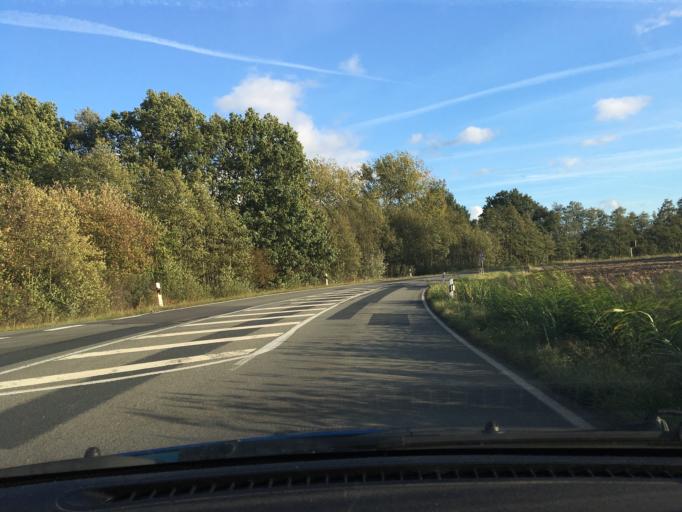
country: DE
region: Lower Saxony
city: Hittbergen
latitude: 53.3419
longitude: 10.6070
